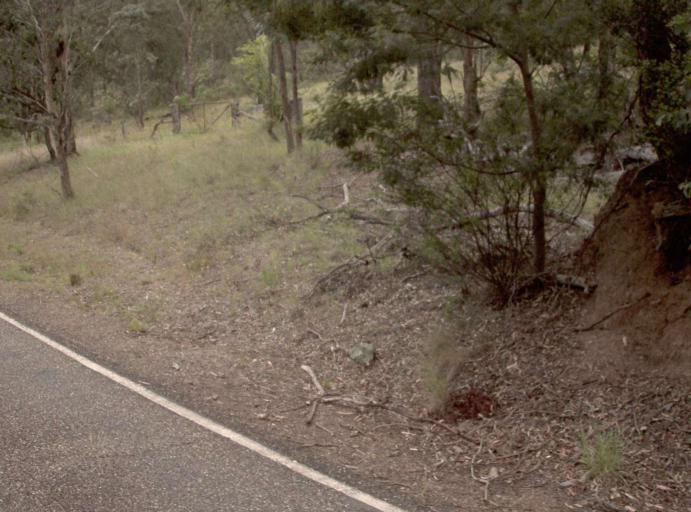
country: AU
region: Victoria
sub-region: East Gippsland
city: Bairnsdale
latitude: -37.5357
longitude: 147.2124
